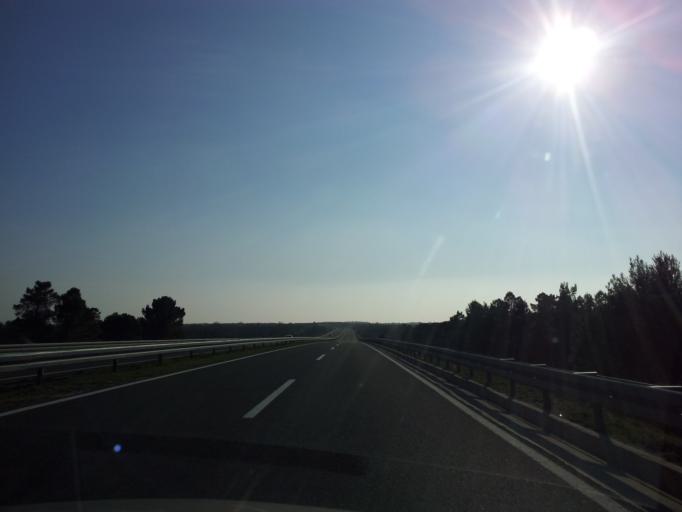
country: HR
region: Zadarska
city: Galovac
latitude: 44.0893
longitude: 15.3615
